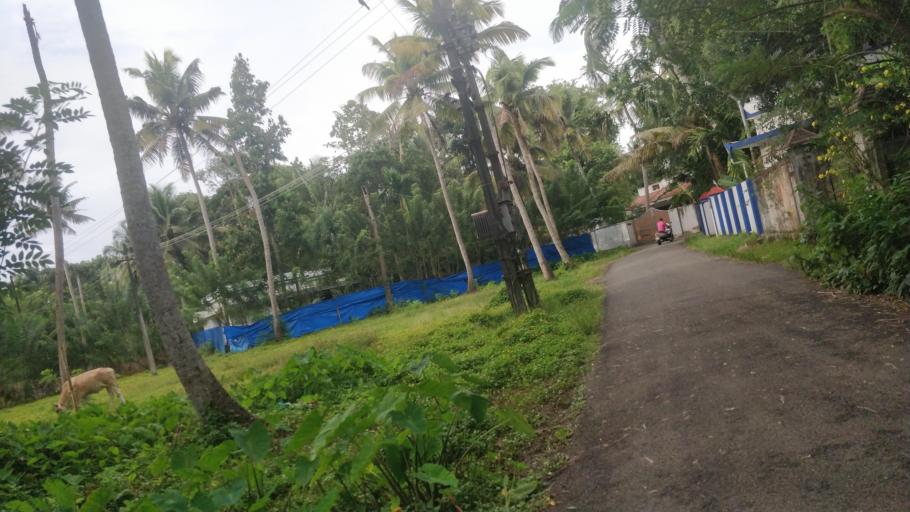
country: IN
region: Kerala
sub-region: Alappuzha
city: Shertallai
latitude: 9.6900
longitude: 76.3597
